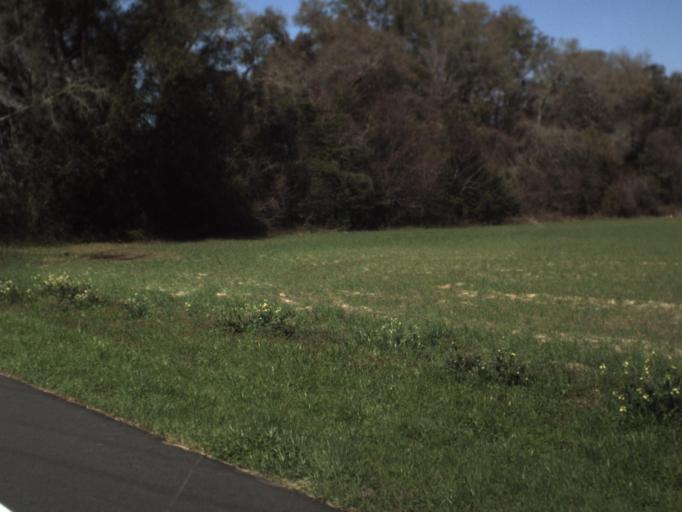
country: US
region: Florida
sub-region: Jackson County
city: Malone
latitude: 30.8550
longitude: -85.0854
